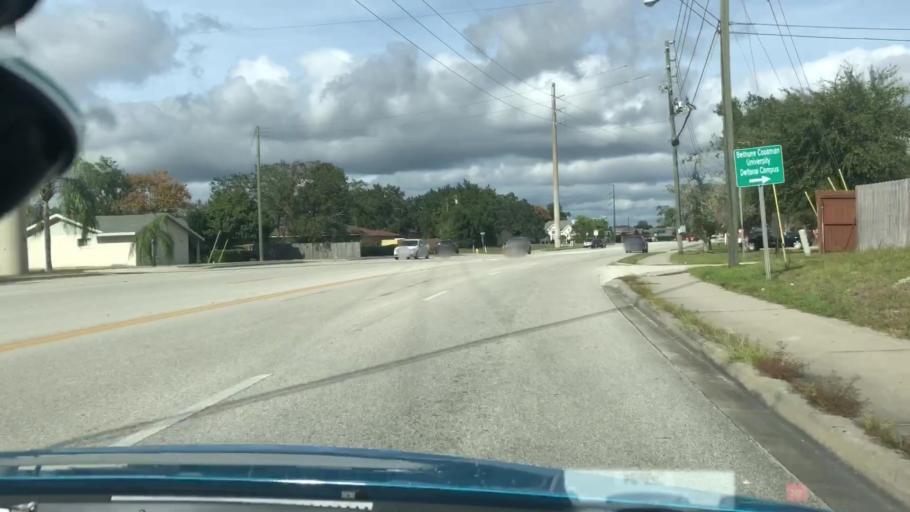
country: US
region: Florida
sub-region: Volusia County
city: Deltona
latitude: 28.9039
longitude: -81.2453
